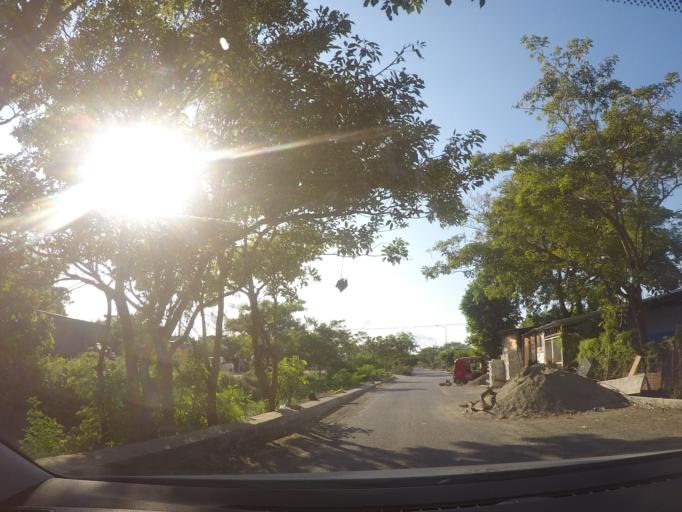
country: MX
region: Oaxaca
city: Juchitan de Zaragoza
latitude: 16.4215
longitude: -95.0281
